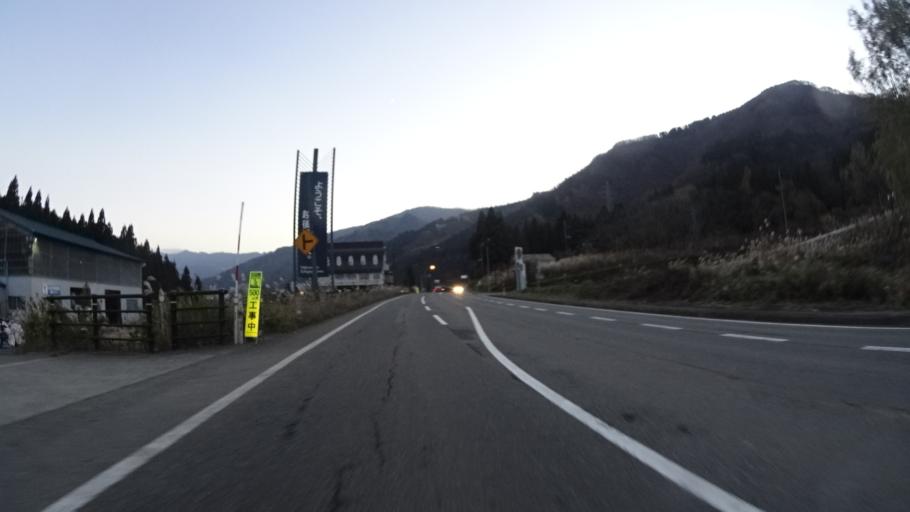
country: JP
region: Niigata
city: Shiozawa
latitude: 36.9634
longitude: 138.8010
